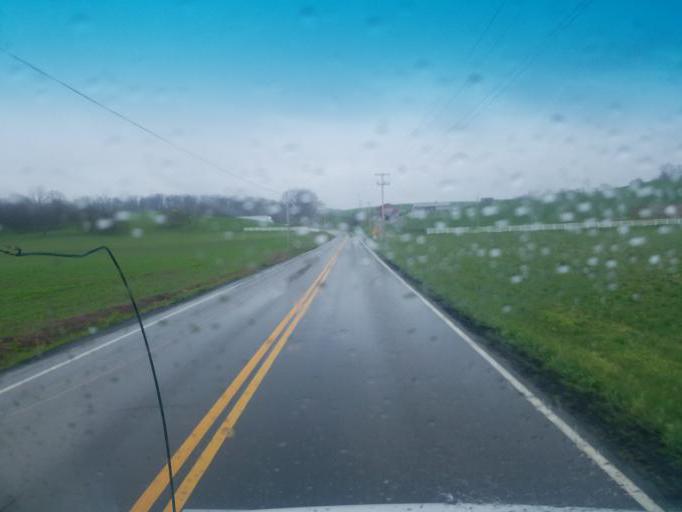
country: US
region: Ohio
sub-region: Holmes County
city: Millersburg
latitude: 40.6271
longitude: -81.9098
